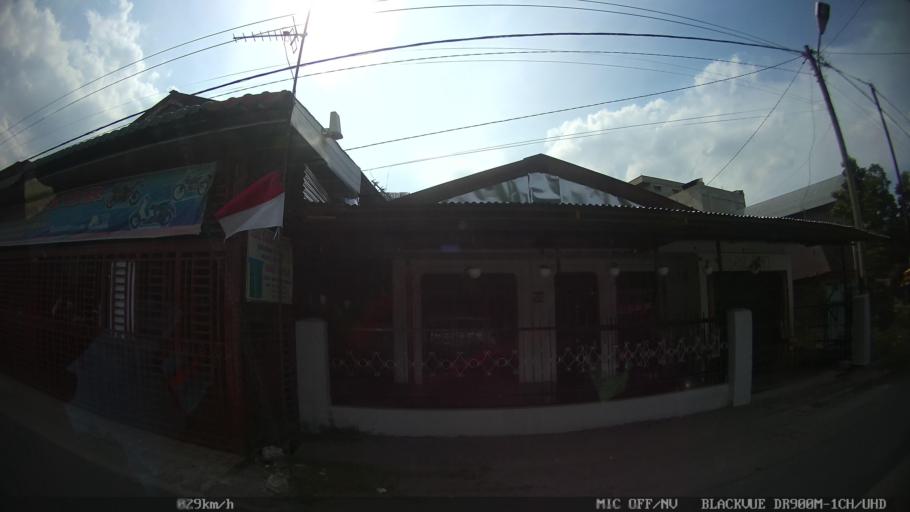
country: ID
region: North Sumatra
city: Binjai
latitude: 3.6115
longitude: 98.4982
